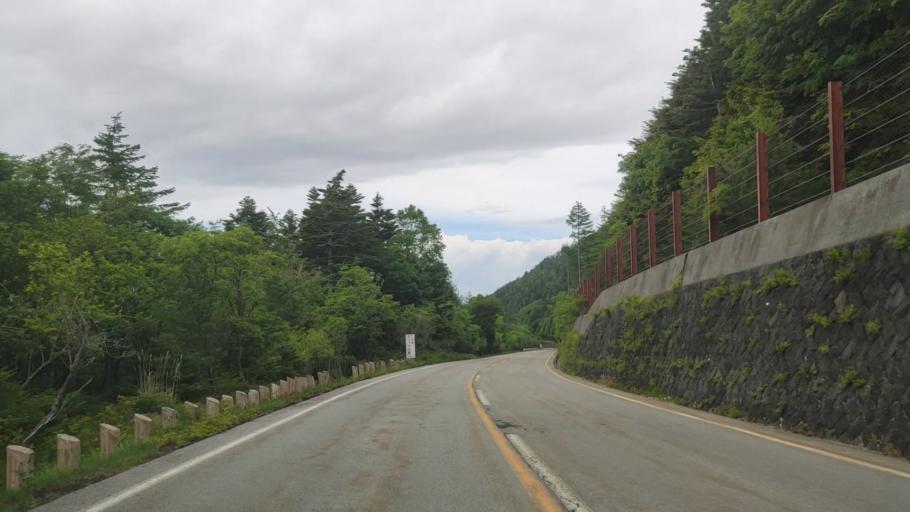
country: JP
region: Yamanashi
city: Fujikawaguchiko
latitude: 35.3916
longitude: 138.6902
